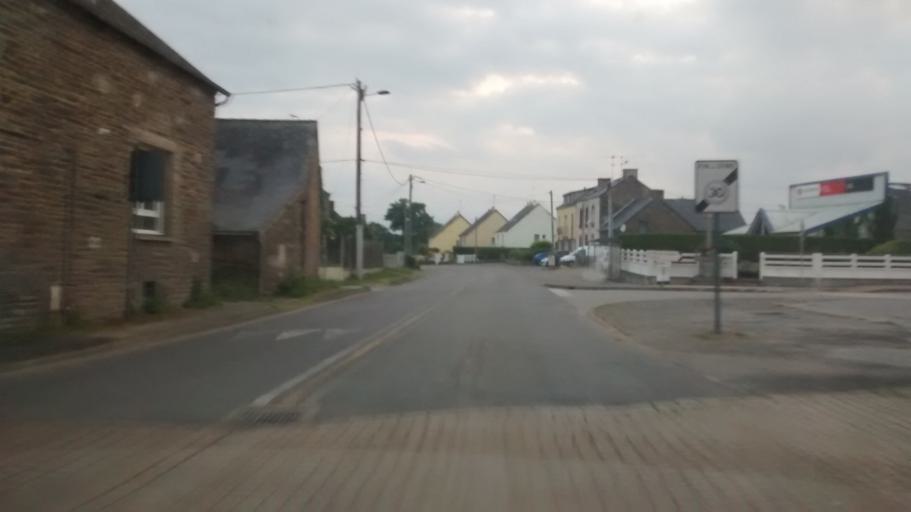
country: FR
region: Brittany
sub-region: Departement du Morbihan
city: Saint-Martin-sur-Oust
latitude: 47.7461
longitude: -2.2558
